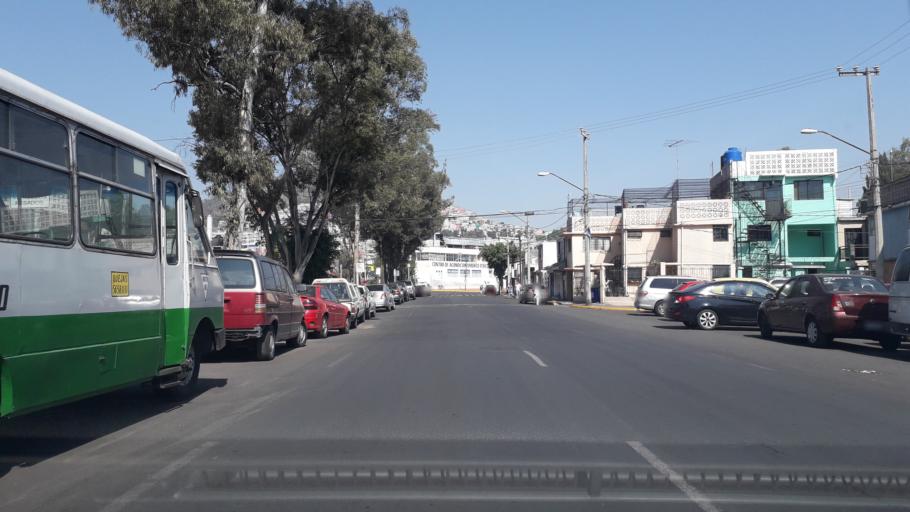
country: MX
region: Mexico City
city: Gustavo A. Madero
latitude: 19.5085
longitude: -99.0983
